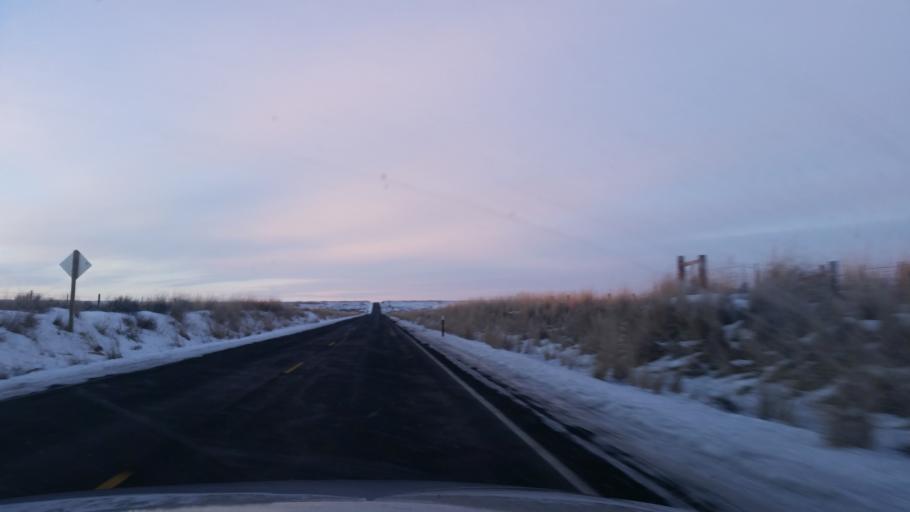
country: US
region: Washington
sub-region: Spokane County
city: Medical Lake
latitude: 47.2143
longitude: -117.8953
